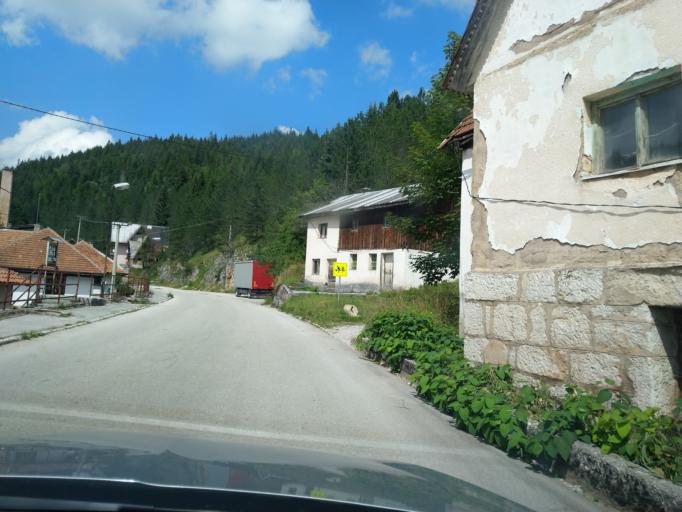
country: RS
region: Central Serbia
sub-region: Zlatiborski Okrug
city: Nova Varos
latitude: 43.5467
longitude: 19.9027
